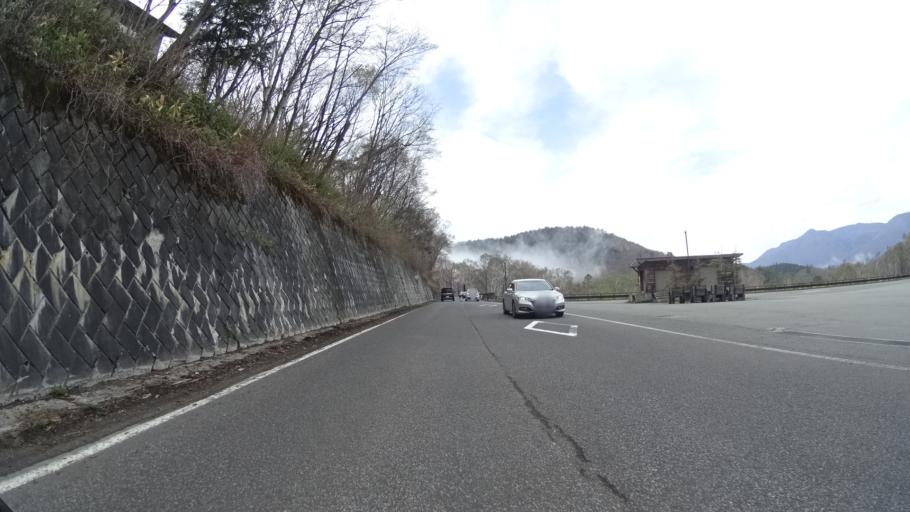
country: JP
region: Nagano
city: Nakano
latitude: 36.7174
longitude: 138.4825
